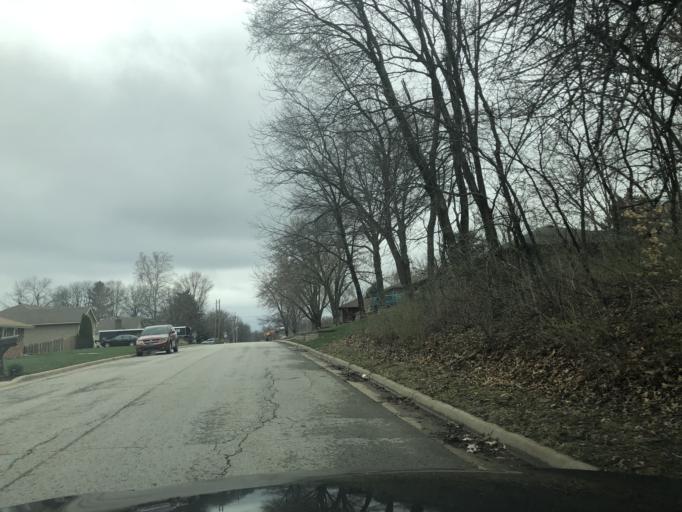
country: US
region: Kansas
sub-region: Leavenworth County
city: Leavenworth
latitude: 39.2801
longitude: -94.9138
